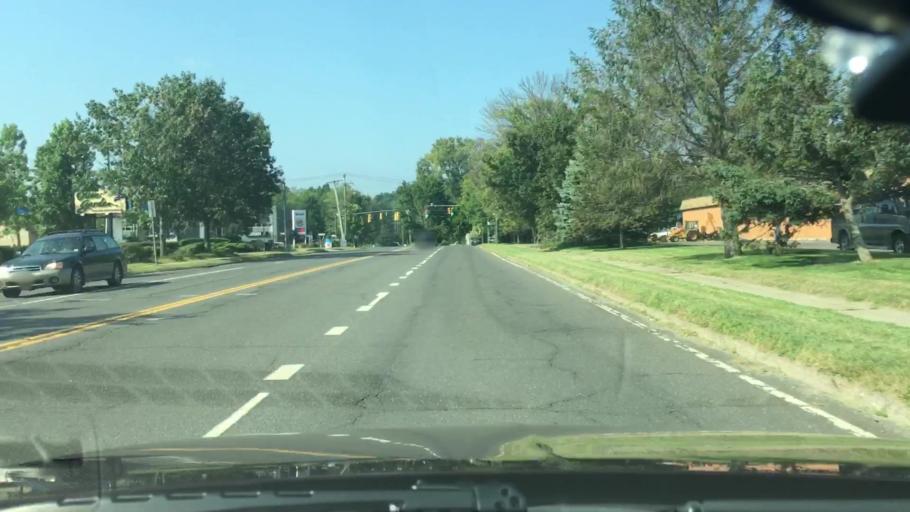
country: US
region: Connecticut
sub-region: Fairfield County
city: Danbury
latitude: 41.3755
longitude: -73.4864
